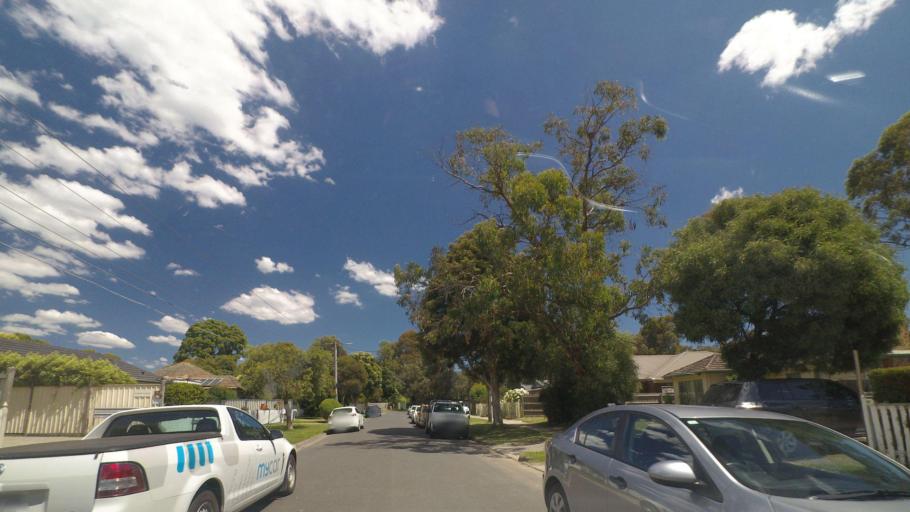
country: AU
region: Victoria
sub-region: Yarra Ranges
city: Kilsyth
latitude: -37.8075
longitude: 145.3124
